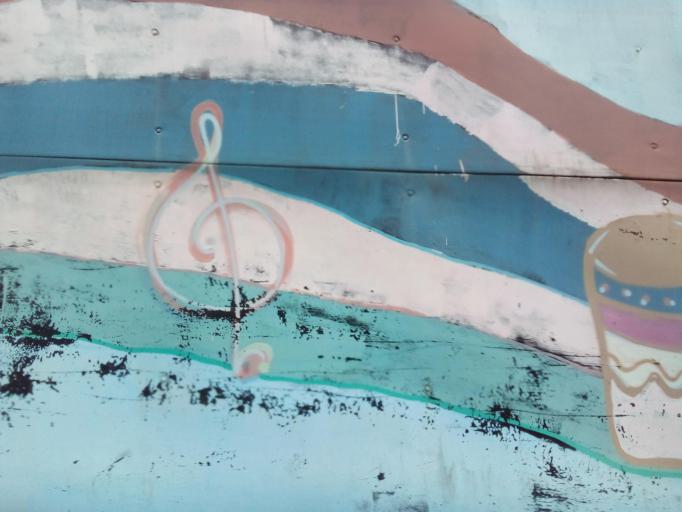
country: BR
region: Espirito Santo
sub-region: Fundao
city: Fundao
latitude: -19.9353
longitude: -40.4042
